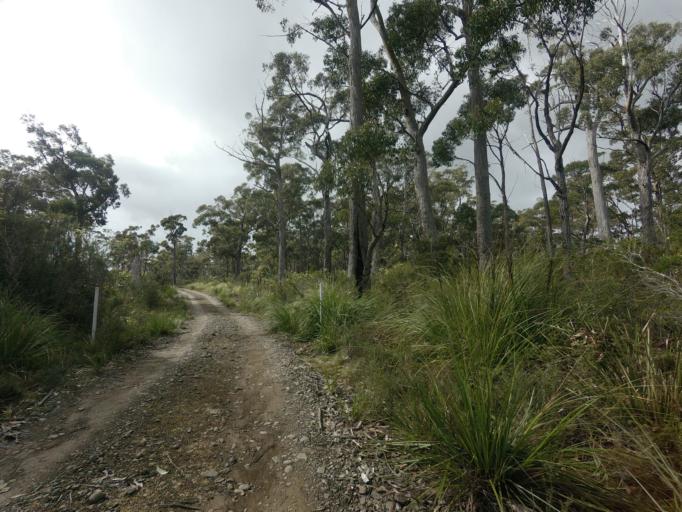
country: AU
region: Tasmania
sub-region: Huon Valley
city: Geeveston
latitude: -43.4615
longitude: 146.9125
